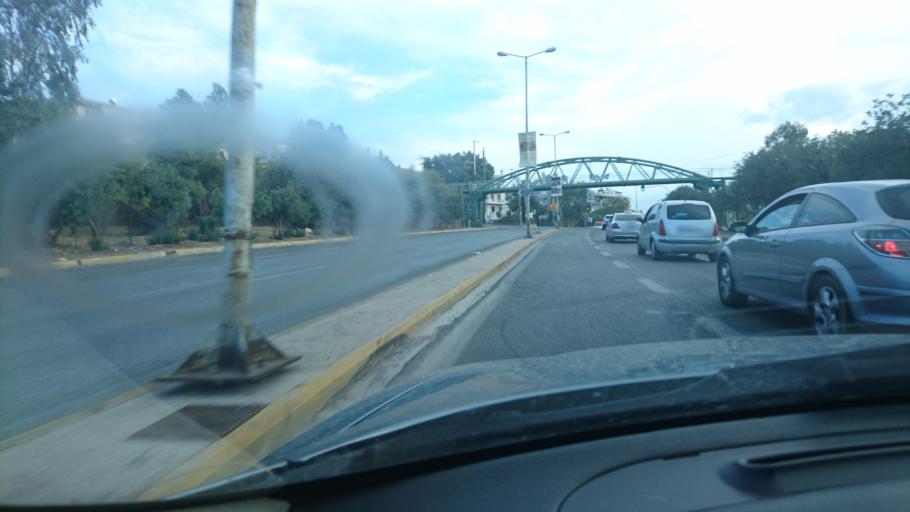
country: GR
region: Attica
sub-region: Nomarchia Athinas
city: Kaisariani
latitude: 37.9502
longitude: 23.7682
